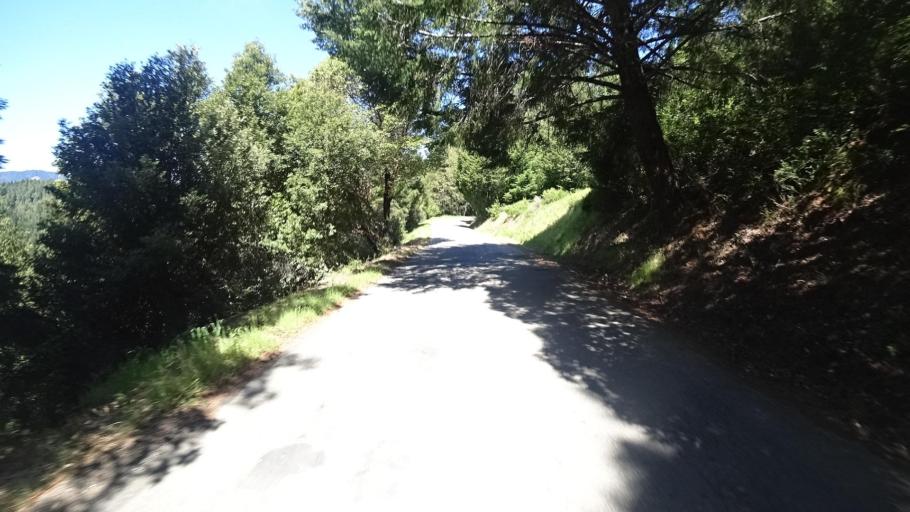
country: US
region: California
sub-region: Humboldt County
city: Redway
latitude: 40.1145
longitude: -123.9657
